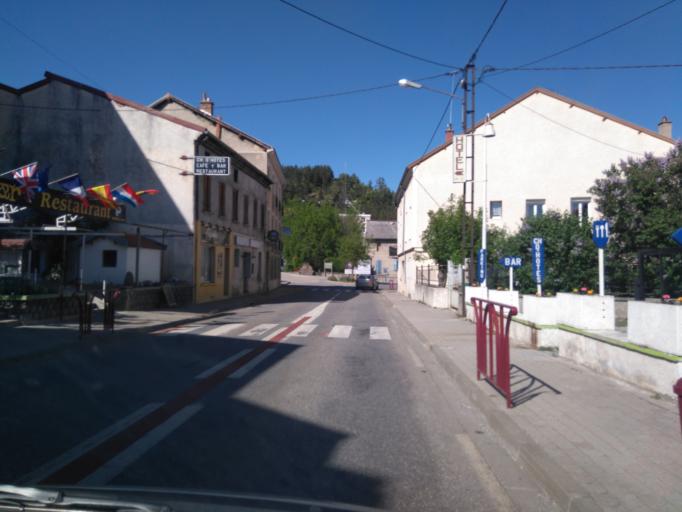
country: FR
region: Provence-Alpes-Cote d'Azur
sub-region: Departement des Hautes-Alpes
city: Veynes
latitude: 44.5218
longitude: 5.7521
